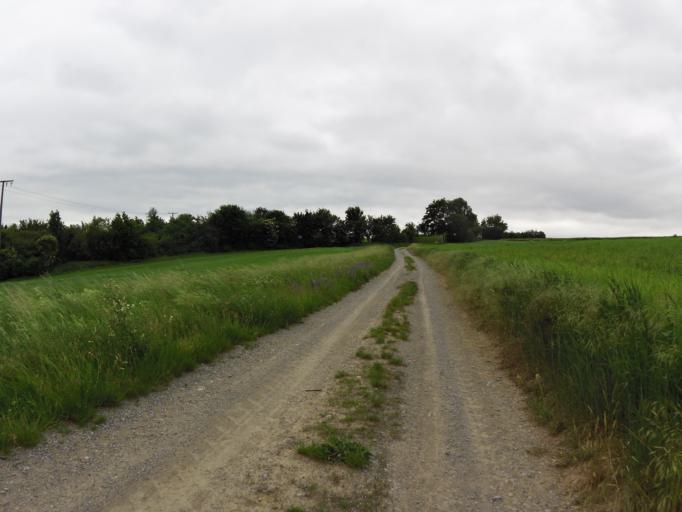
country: DE
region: Bavaria
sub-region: Regierungsbezirk Unterfranken
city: Zell am Main
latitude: 49.8151
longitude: 9.8553
